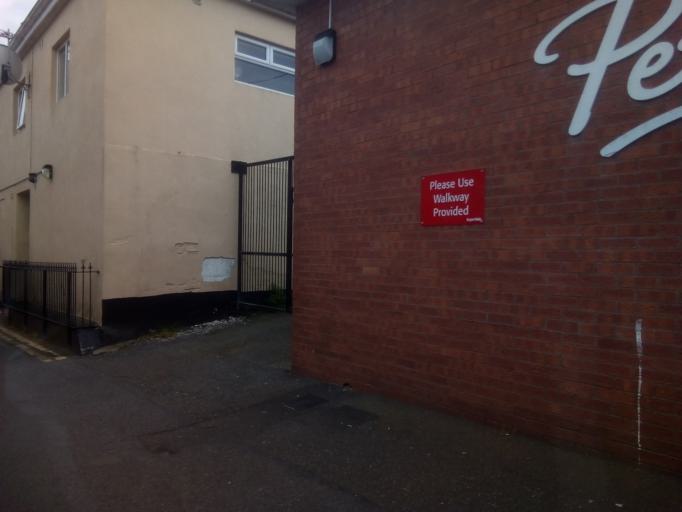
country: IE
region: Leinster
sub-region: Loch Garman
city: Gorey
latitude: 52.6767
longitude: -6.2945
